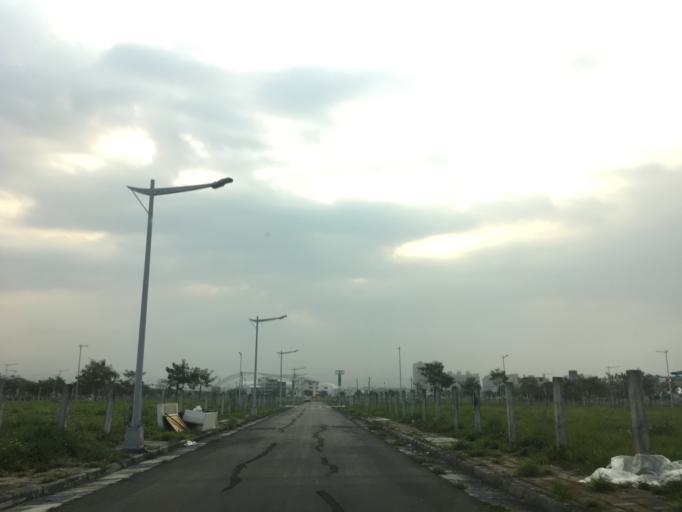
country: TW
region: Taiwan
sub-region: Taichung City
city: Taichung
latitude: 24.1986
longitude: 120.6726
